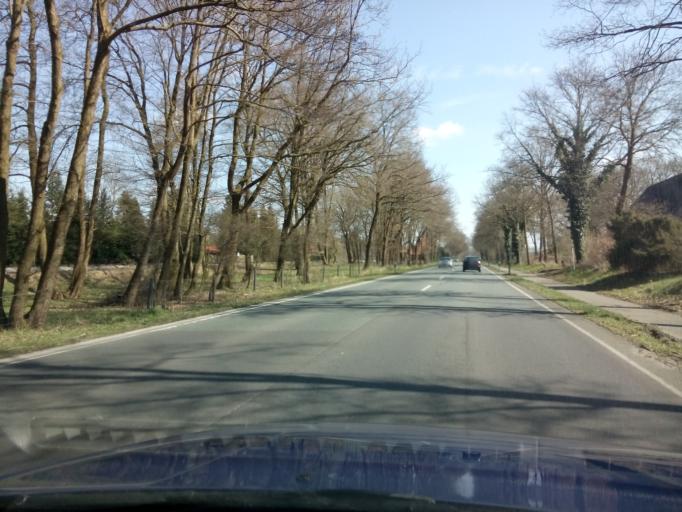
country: DE
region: Lower Saxony
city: Emlichheim
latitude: 52.6103
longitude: 6.8264
